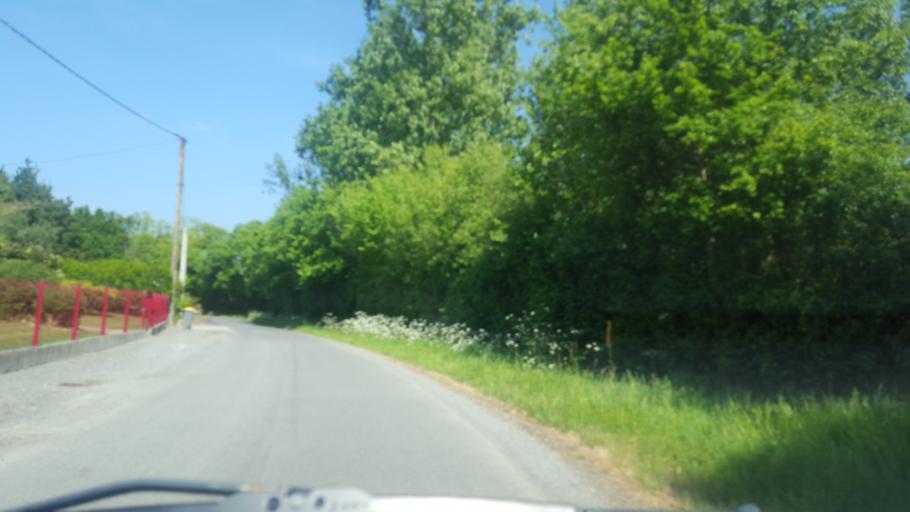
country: FR
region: Pays de la Loire
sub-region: Departement de la Loire-Atlantique
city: La Limouziniere
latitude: 47.0396
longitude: -1.5816
